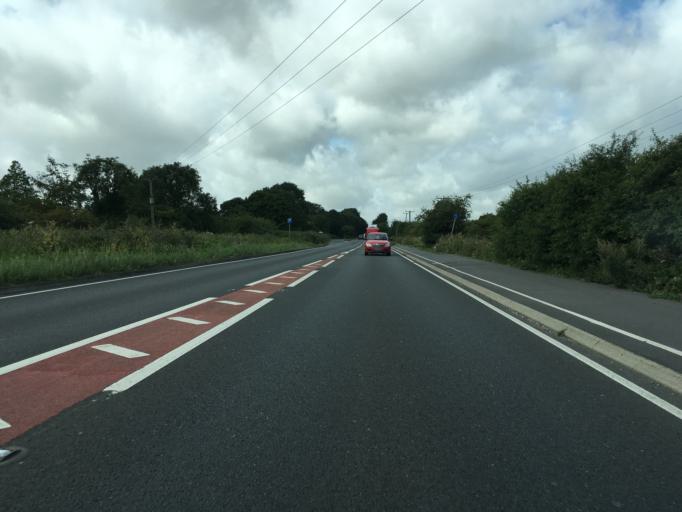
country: GB
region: England
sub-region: East Sussex
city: Ringmer
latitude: 50.8535
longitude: 0.0917
